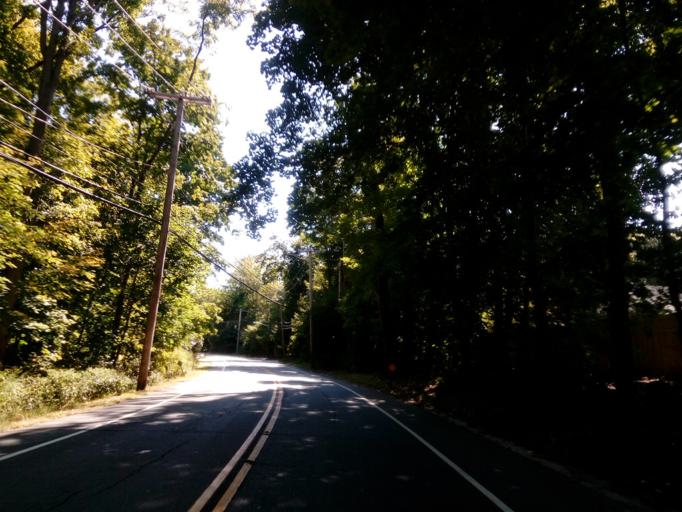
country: US
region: New York
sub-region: Nassau County
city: Oyster Bay Cove
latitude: 40.8631
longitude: -73.4969
